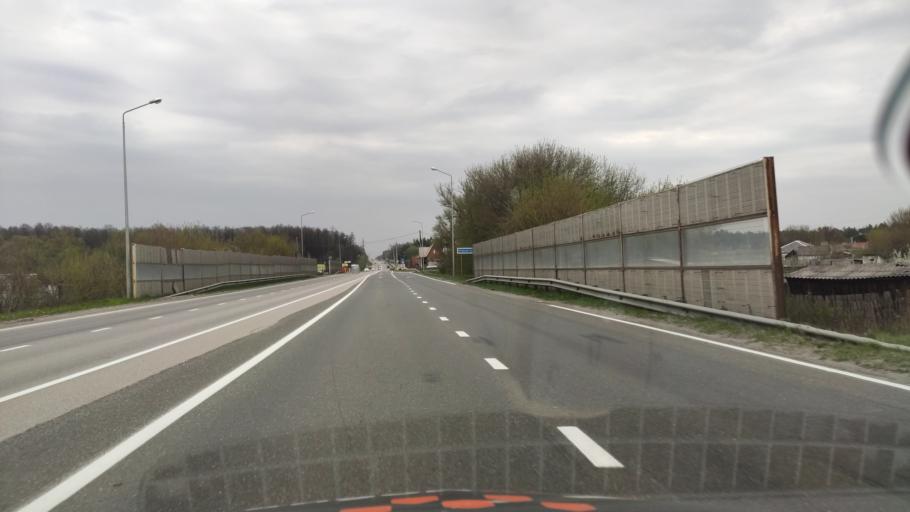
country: RU
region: Belgorod
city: Staryy Oskol
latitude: 51.3526
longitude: 37.8298
